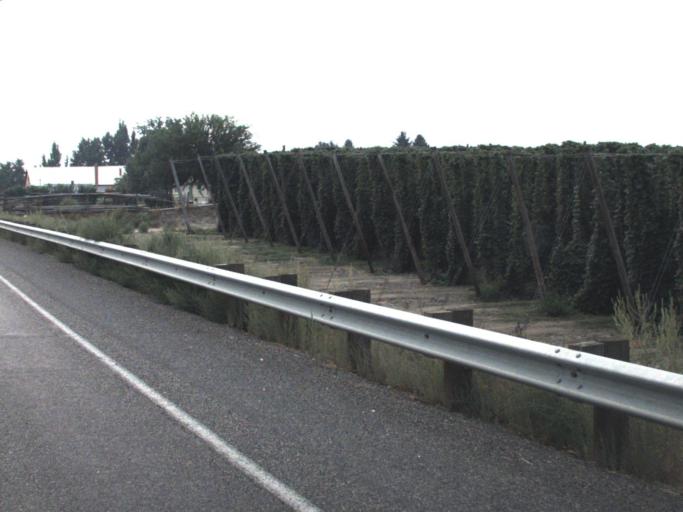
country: US
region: Washington
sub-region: Yakima County
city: Mabton
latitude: 46.2625
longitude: -119.9994
